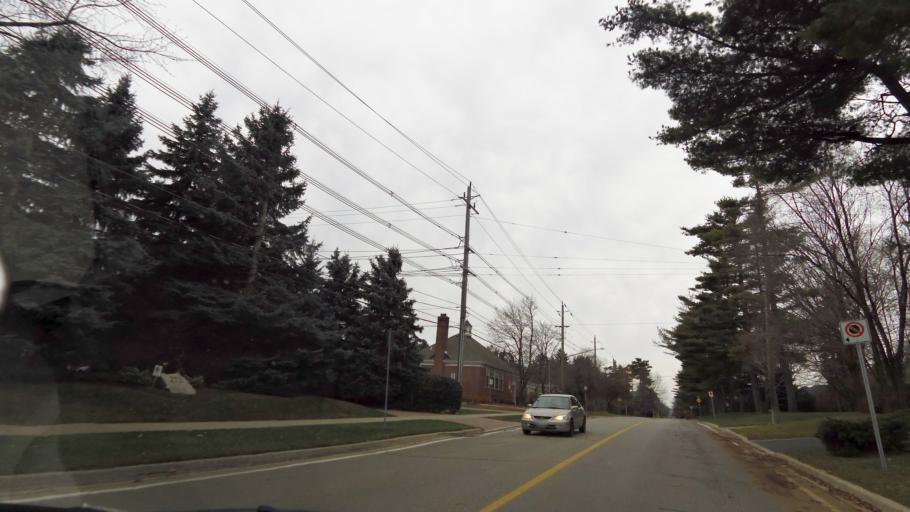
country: CA
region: Ontario
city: Oakville
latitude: 43.4732
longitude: -79.6494
